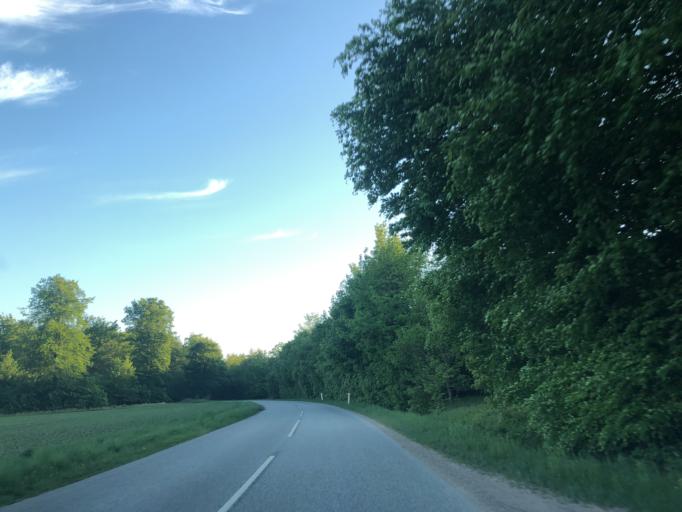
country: DK
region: Zealand
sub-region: Koge Kommune
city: Borup
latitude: 55.4353
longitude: 11.9413
